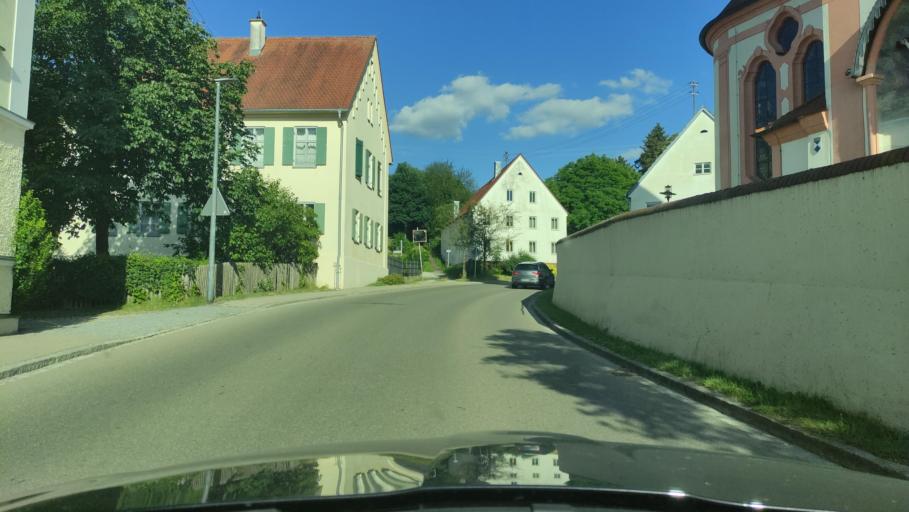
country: DE
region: Bavaria
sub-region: Swabia
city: Deisenhausen
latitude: 48.2561
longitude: 10.3247
